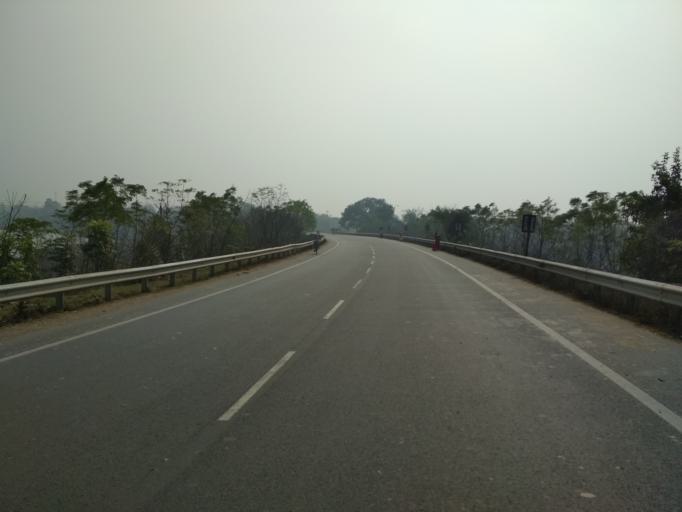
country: IN
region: Bihar
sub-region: Khagaria
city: Khagaria
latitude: 25.4952
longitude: 86.5954
